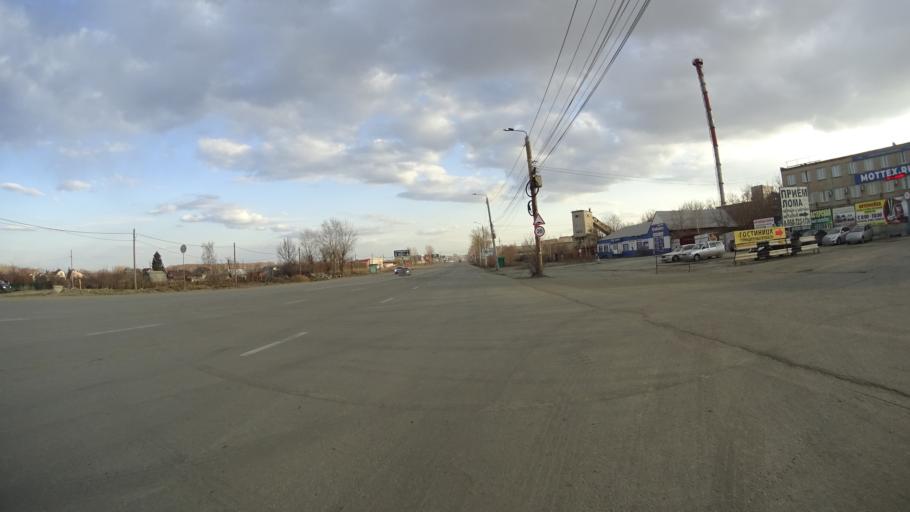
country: RU
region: Chelyabinsk
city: Novosineglazovskiy
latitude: 55.0988
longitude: 61.3876
